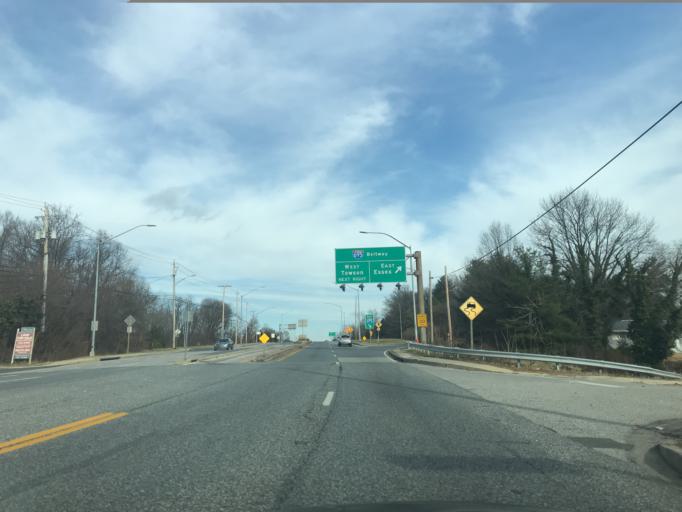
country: US
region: Maryland
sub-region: Baltimore County
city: Overlea
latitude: 39.3674
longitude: -76.5162
